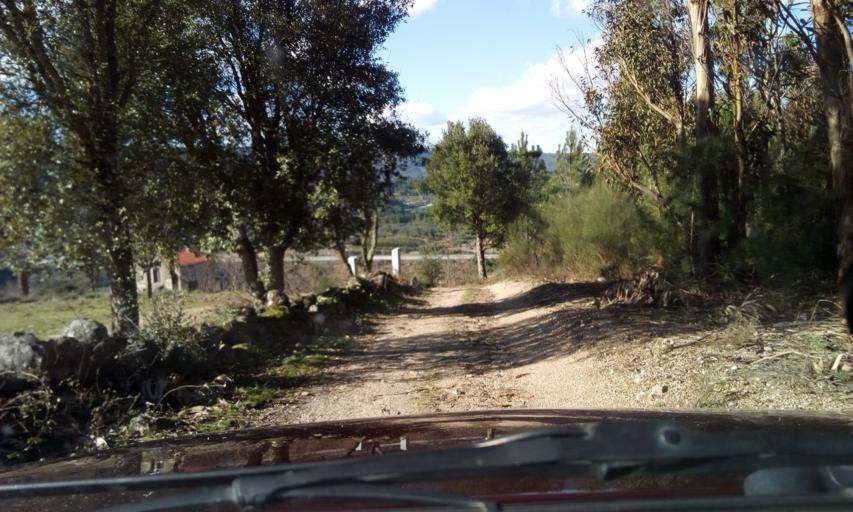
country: PT
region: Guarda
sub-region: Fornos de Algodres
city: Fornos de Algodres
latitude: 40.6123
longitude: -7.5046
